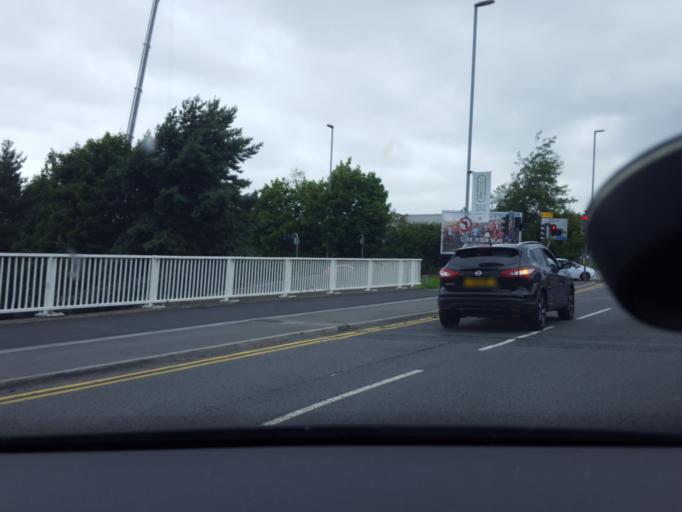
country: GB
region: England
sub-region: City and Borough of Leeds
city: Horsforth
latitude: 53.8042
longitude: -1.6209
